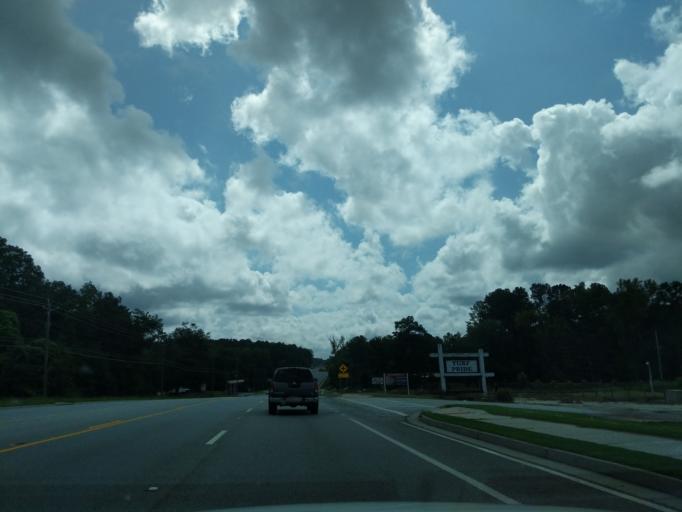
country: US
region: Georgia
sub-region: Columbia County
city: Evans
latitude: 33.5561
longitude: -82.1591
